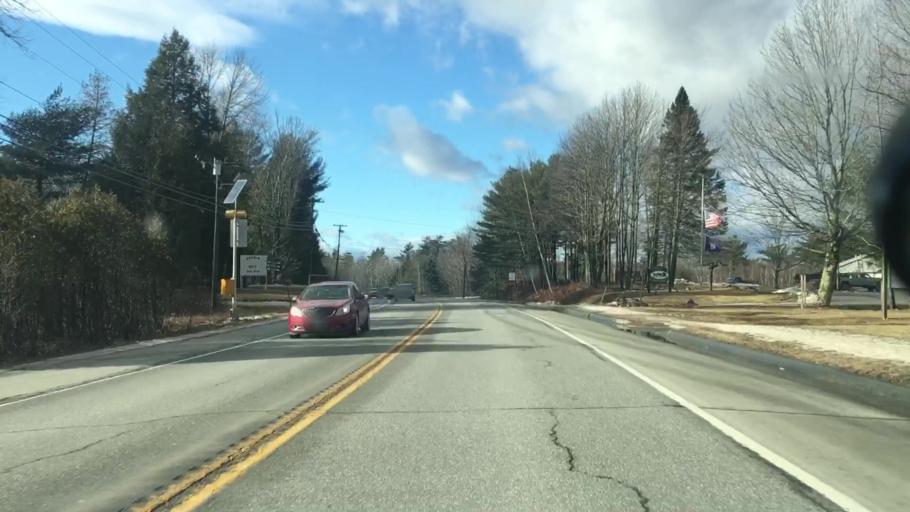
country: US
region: Maine
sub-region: Penobscot County
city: Holden
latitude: 44.7552
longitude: -68.6622
